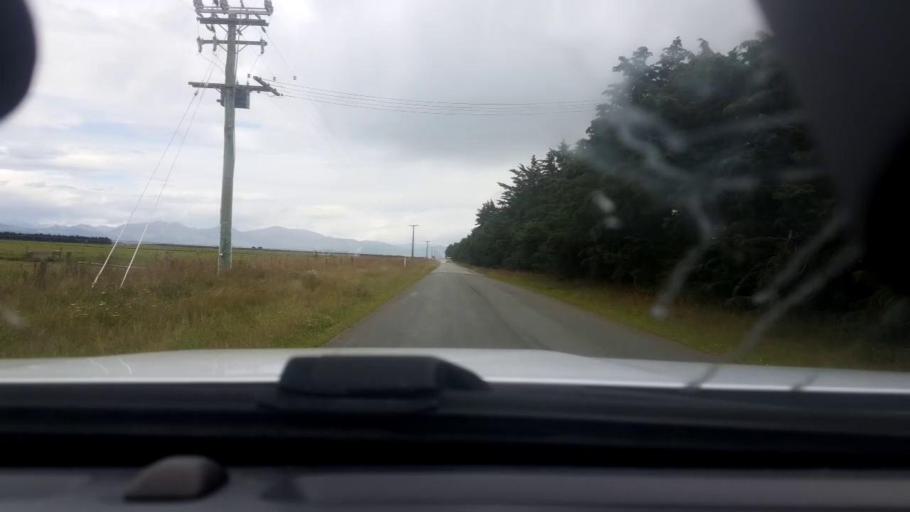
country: NZ
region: Canterbury
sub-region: Timaru District
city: Timaru
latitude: -44.1584
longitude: 171.4021
